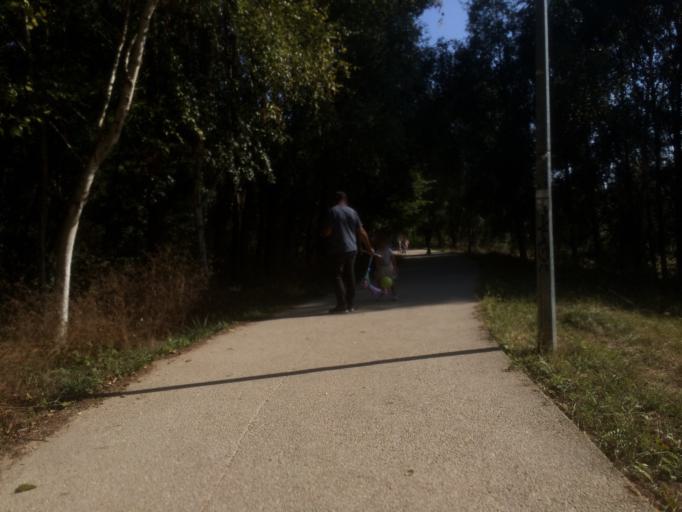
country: FR
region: Ile-de-France
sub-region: Departement de l'Essonne
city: Longjumeau
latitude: 48.6880
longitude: 2.3160
